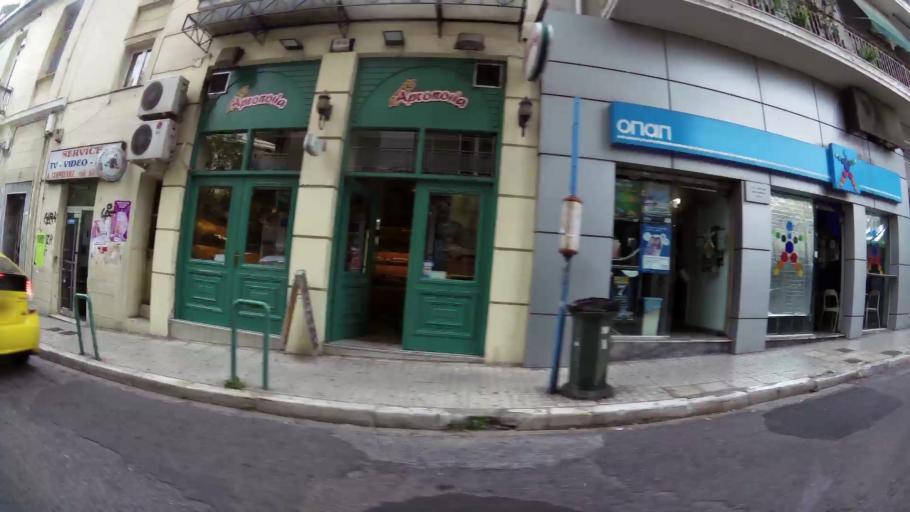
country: GR
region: Attica
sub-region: Nomarchia Athinas
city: Kipseli
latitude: 37.9924
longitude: 23.7488
